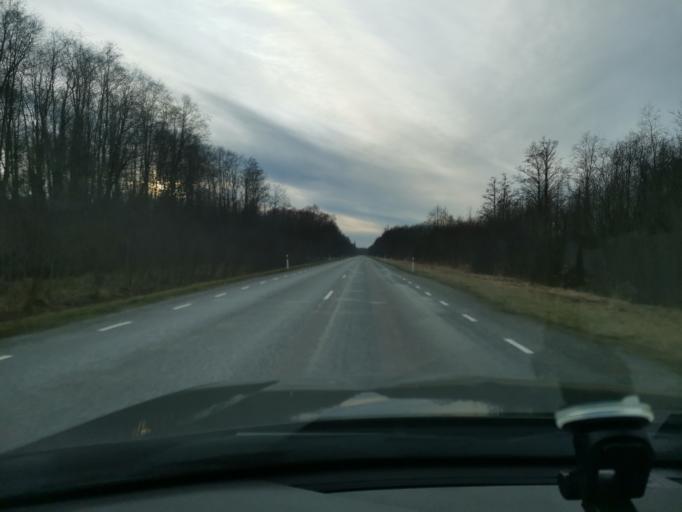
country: EE
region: Ida-Virumaa
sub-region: Narva-Joesuu linn
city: Narva-Joesuu
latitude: 59.3281
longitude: 27.9354
